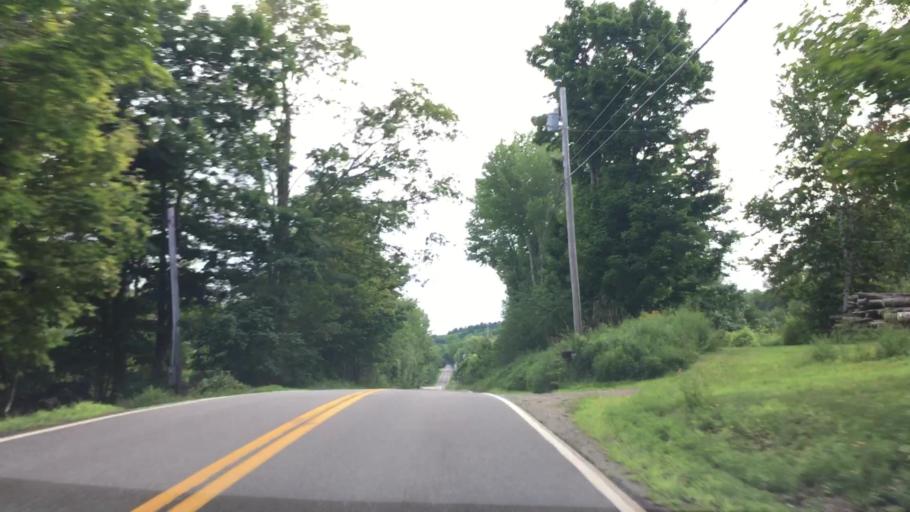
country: US
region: Maine
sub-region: Waldo County
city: Belfast
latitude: 44.3596
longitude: -69.0469
